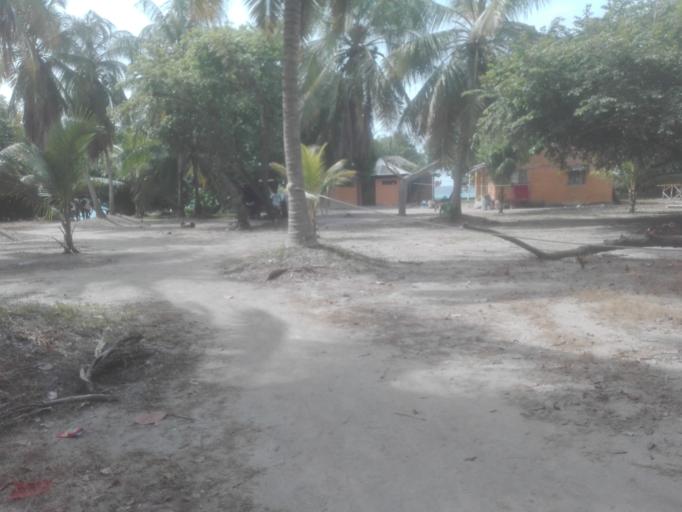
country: CO
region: Bolivar
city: Turbana
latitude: 10.1805
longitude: -75.7315
